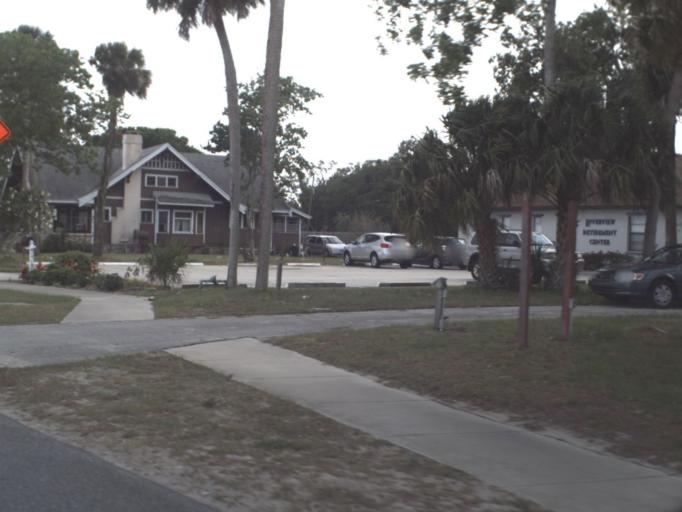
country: US
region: Florida
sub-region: Brevard County
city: Titusville
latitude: 28.5600
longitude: -80.7987
